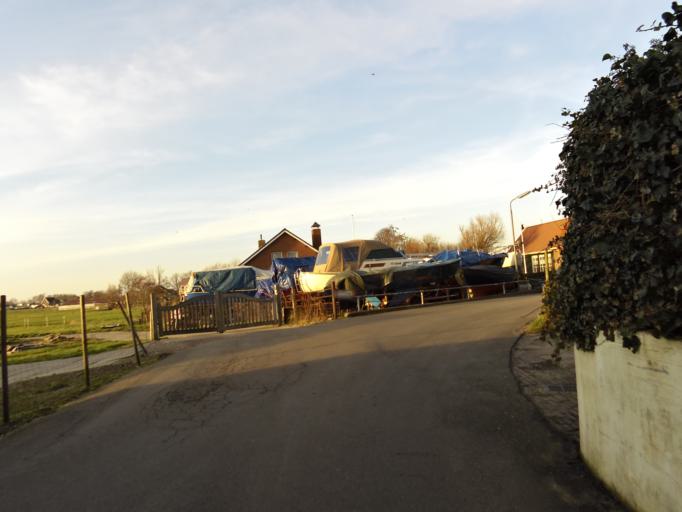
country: NL
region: South Holland
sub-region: Gemeente Teylingen
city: Sassenheim
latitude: 52.1950
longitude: 4.5574
